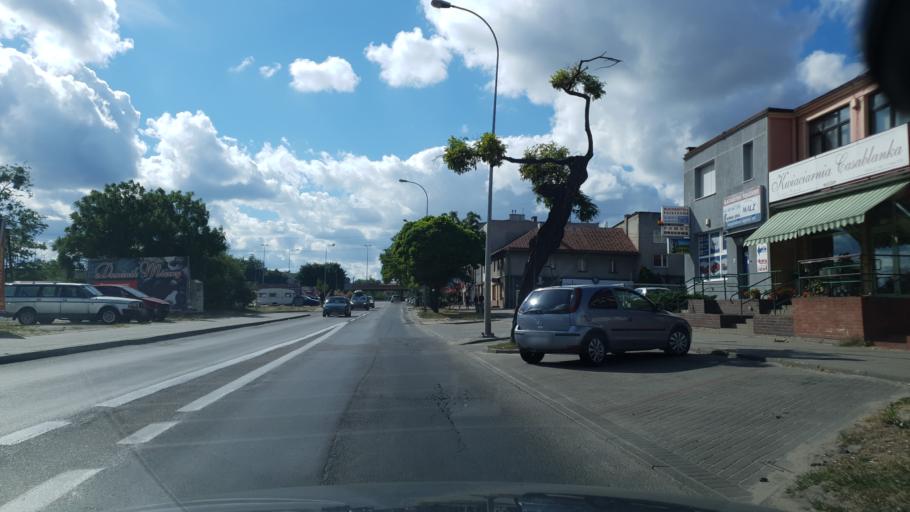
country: PL
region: Pomeranian Voivodeship
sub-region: Gdynia
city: Pogorze
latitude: 54.5504
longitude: 18.5111
